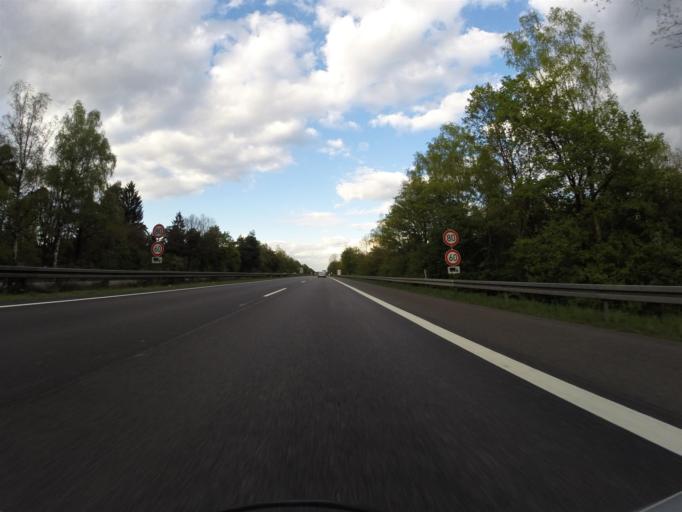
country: DE
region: Rheinland-Pfalz
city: Waldmohr
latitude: 49.3593
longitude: 7.3351
